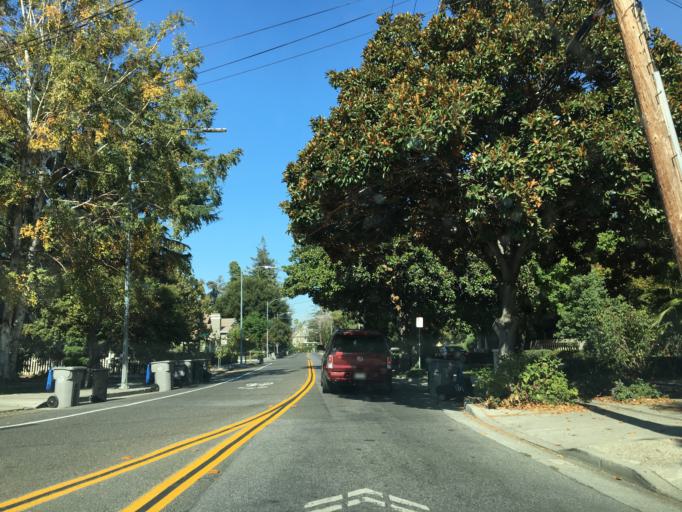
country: US
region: California
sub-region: Santa Clara County
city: Buena Vista
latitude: 37.3117
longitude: -121.8965
